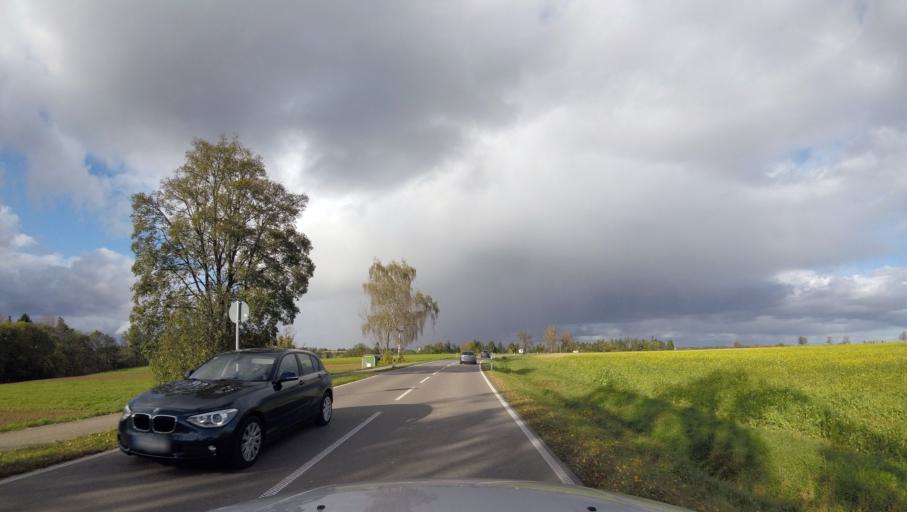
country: DE
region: Baden-Wuerttemberg
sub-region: Regierungsbezirk Stuttgart
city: Alfdorf
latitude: 48.8008
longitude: 9.7449
